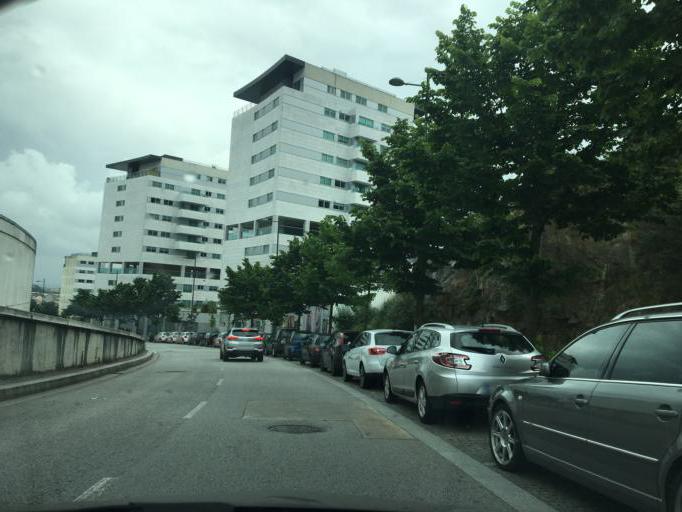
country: PT
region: Porto
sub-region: Porto
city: Porto
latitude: 41.1614
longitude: -8.5854
